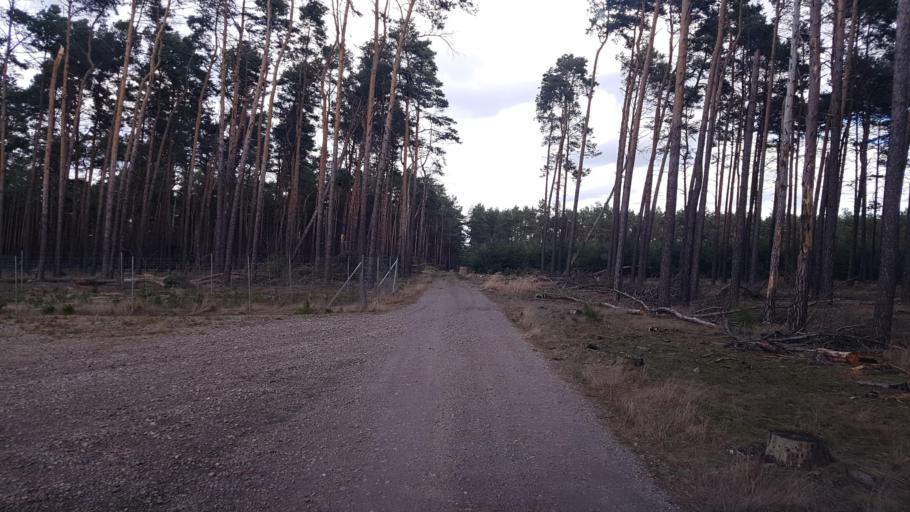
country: DE
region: Brandenburg
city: Schlieben
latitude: 51.6694
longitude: 13.3964
